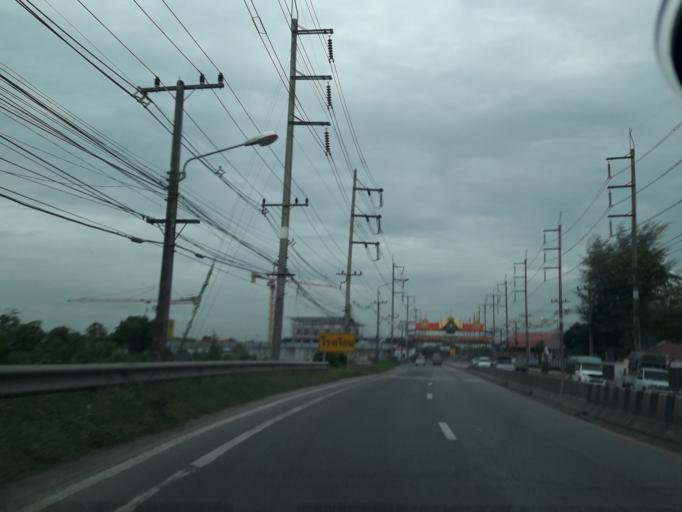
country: TH
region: Pathum Thani
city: Lam Luk Ka
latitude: 13.9409
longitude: 100.7666
